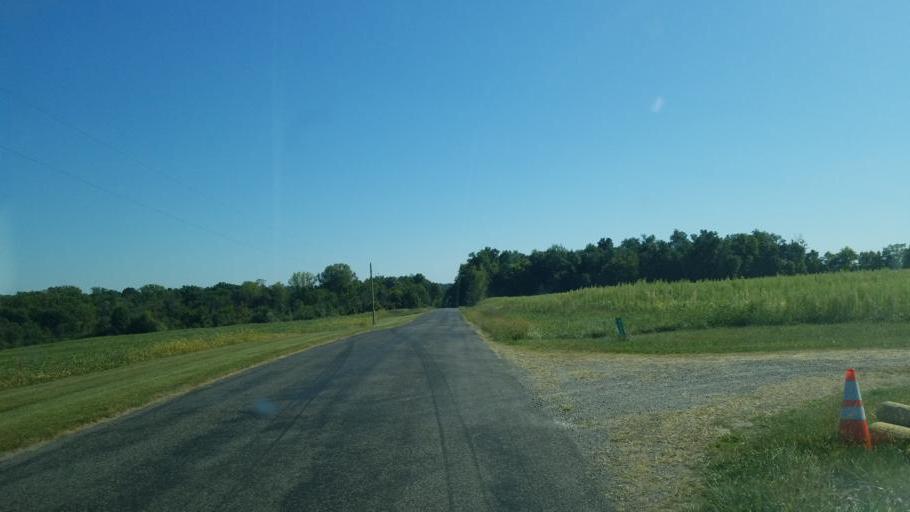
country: US
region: Ohio
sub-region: Champaign County
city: North Lewisburg
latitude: 40.1812
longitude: -83.6156
